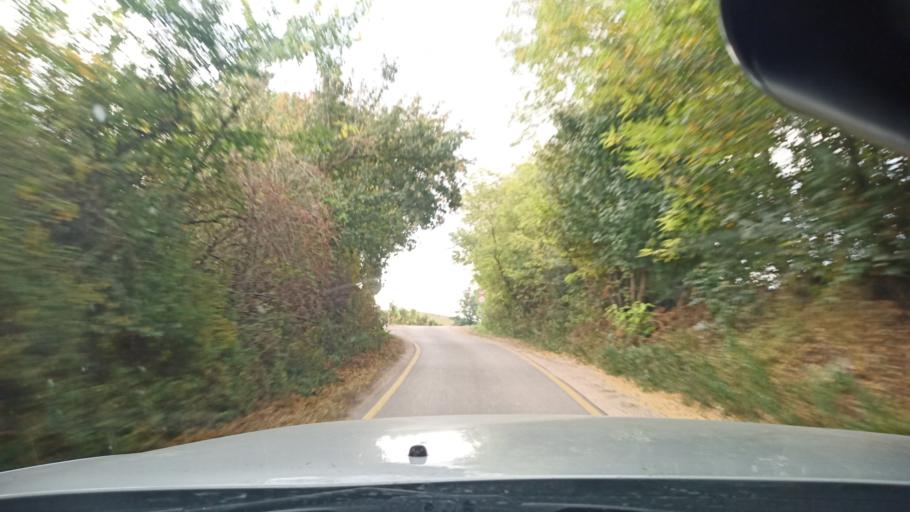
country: HU
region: Fejer
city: Mor
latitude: 47.3710
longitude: 18.2402
